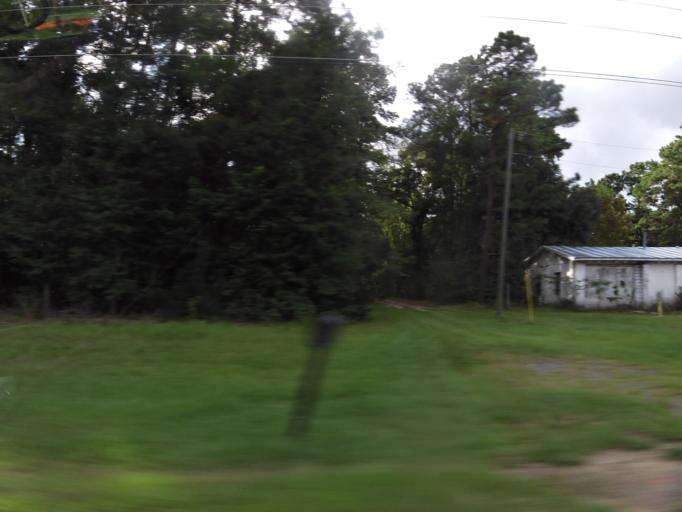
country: US
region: Georgia
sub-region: Liberty County
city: Midway
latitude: 31.7853
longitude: -81.4374
